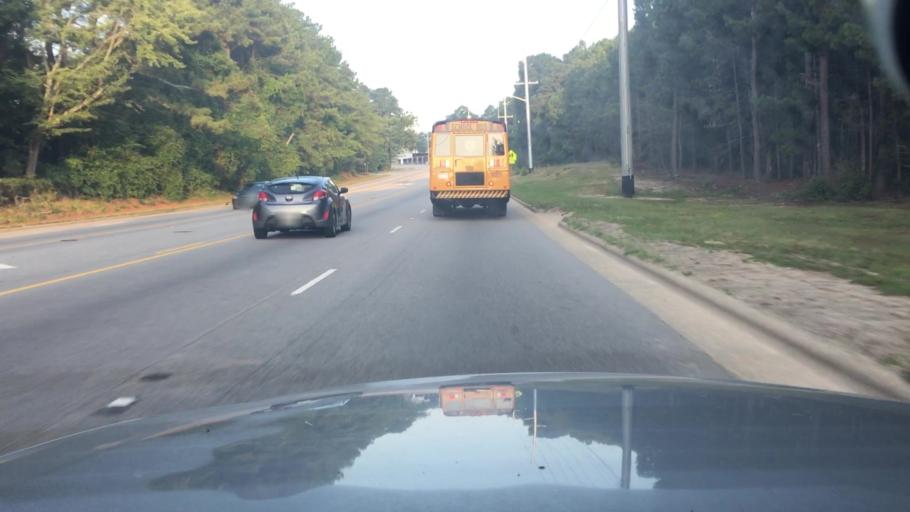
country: US
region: North Carolina
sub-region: Cumberland County
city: Fayetteville
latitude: 35.1006
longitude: -78.9087
